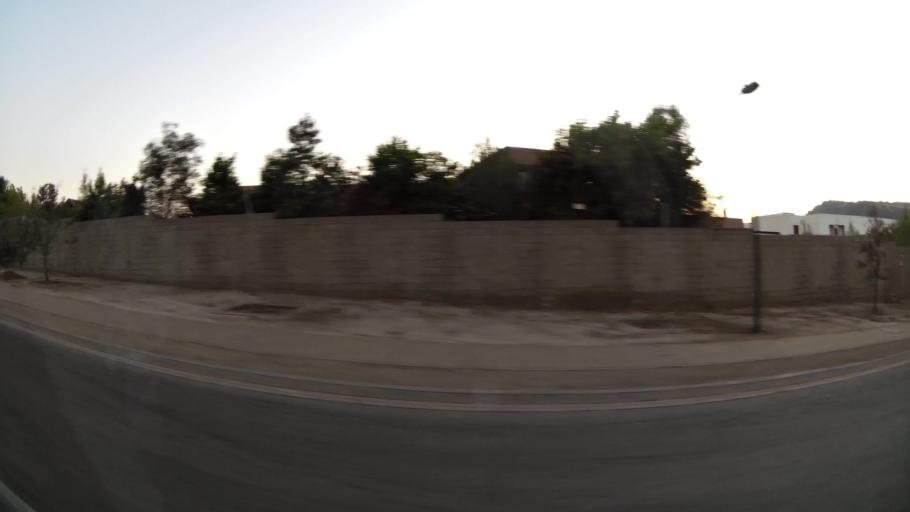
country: CL
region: Santiago Metropolitan
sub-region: Provincia de Chacabuco
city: Chicureo Abajo
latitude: -33.3216
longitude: -70.5436
